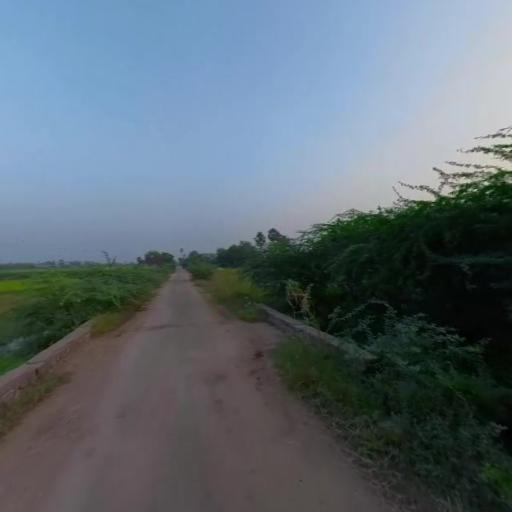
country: IN
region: Telangana
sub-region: Nalgonda
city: Suriapet
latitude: 17.0638
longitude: 79.5471
